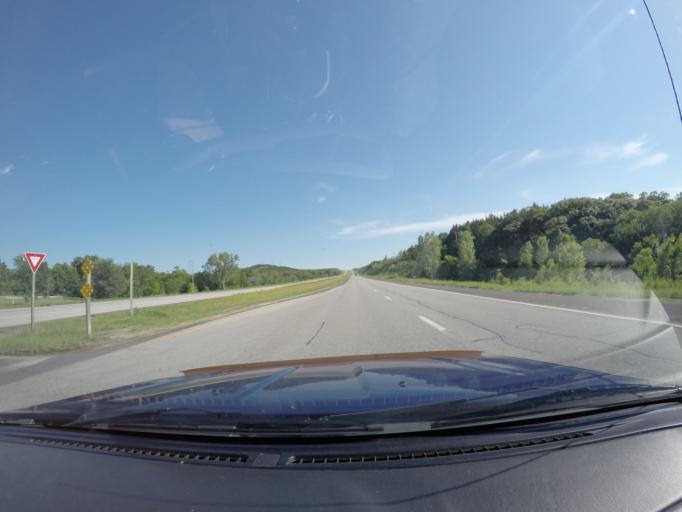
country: US
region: Kansas
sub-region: Riley County
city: Manhattan
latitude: 39.1554
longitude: -96.5385
